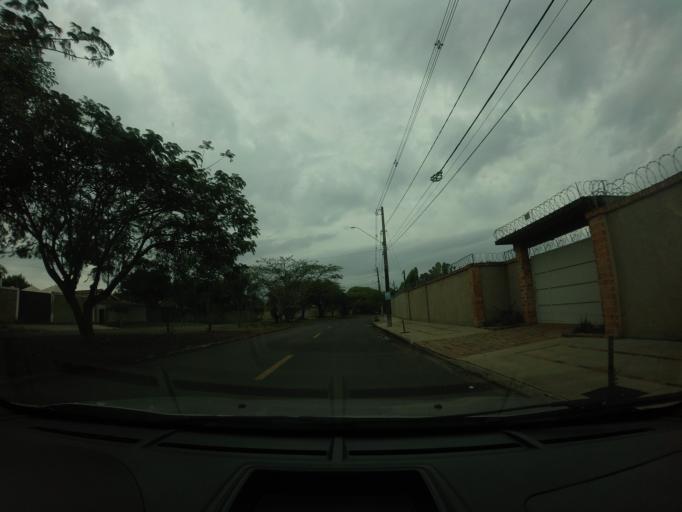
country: BR
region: Sao Paulo
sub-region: Piracicaba
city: Piracicaba
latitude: -22.7629
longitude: -47.5927
